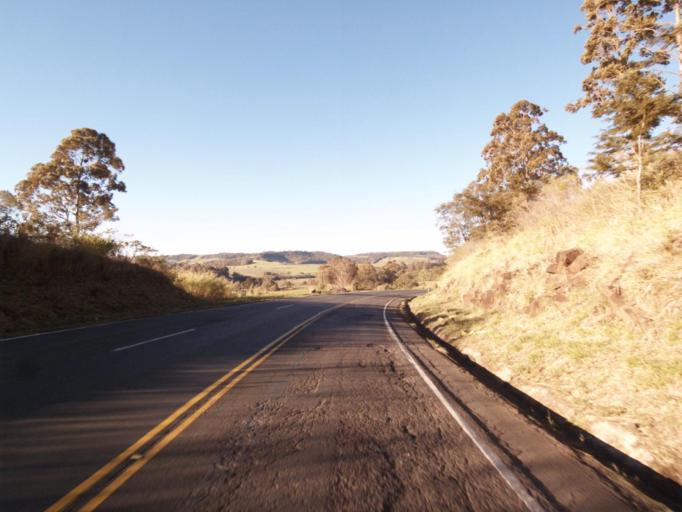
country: AR
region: Misiones
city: Bernardo de Irigoyen
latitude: -26.3294
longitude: -53.5445
